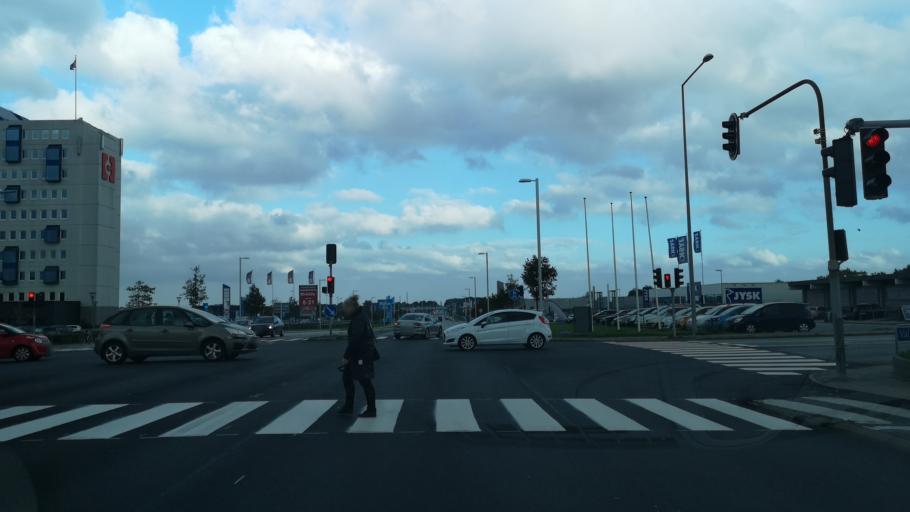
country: DK
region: Central Jutland
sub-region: Herning Kommune
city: Herning
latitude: 56.1346
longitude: 8.9989
